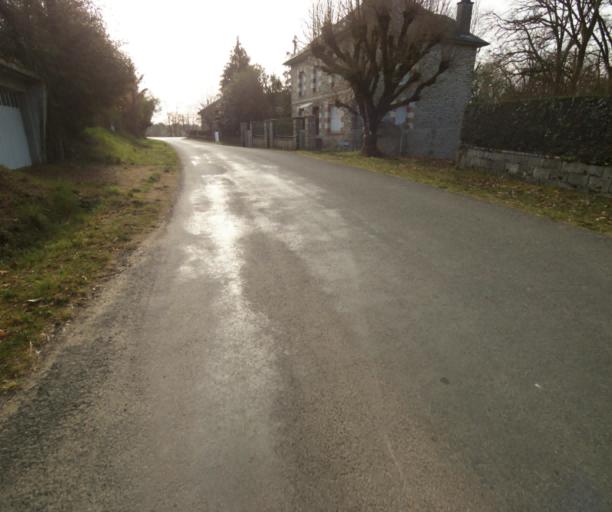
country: FR
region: Limousin
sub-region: Departement de la Correze
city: Chamboulive
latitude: 45.4329
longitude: 1.7659
